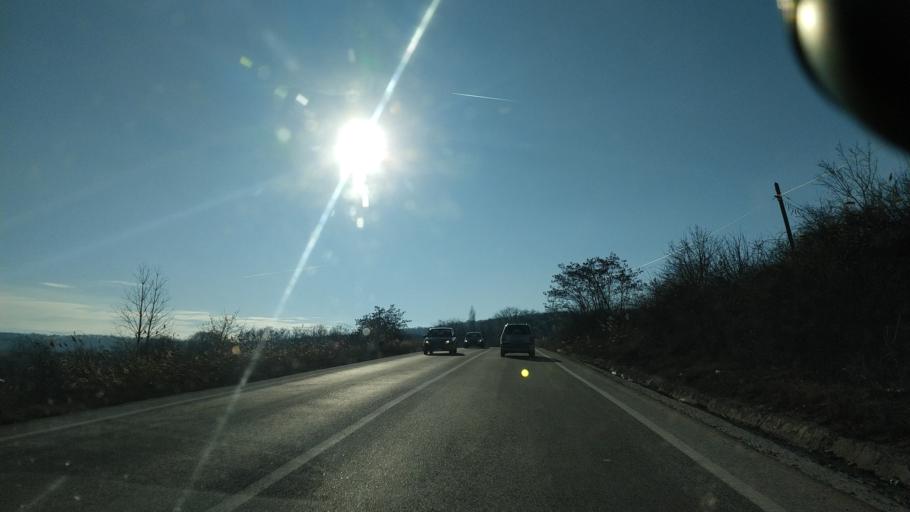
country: RO
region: Iasi
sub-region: Comuna Strunga
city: Strunga
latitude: 47.1780
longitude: 26.9546
